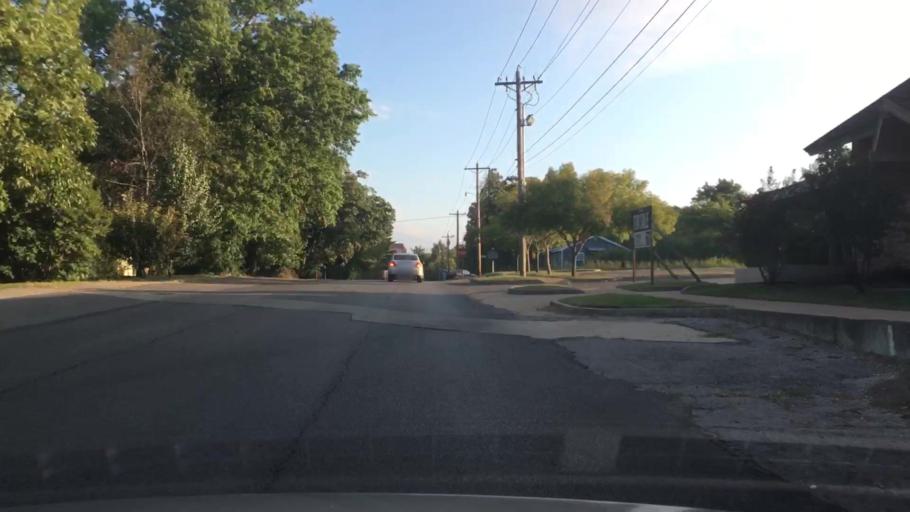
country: US
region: Oklahoma
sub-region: Cherokee County
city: Tahlequah
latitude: 35.9152
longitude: -94.9716
